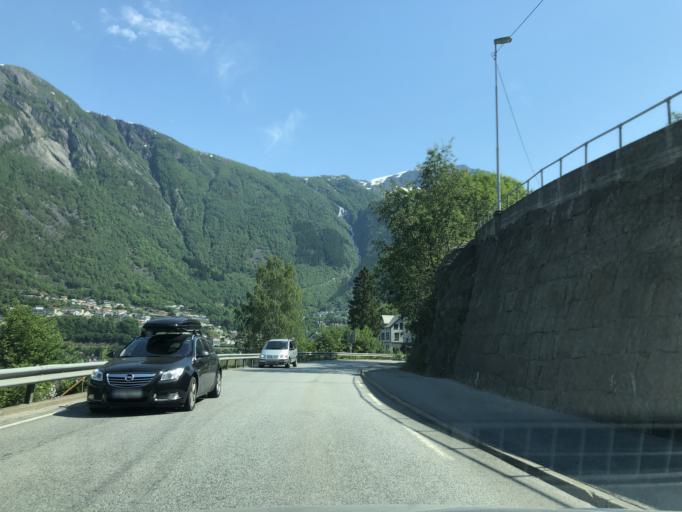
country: NO
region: Hordaland
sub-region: Odda
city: Odda
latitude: 60.0762
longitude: 6.5337
